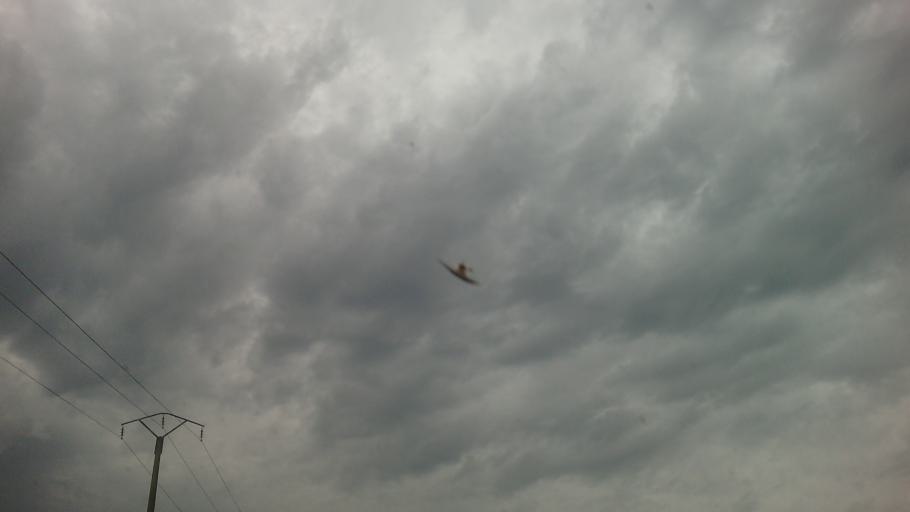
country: BJ
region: Mono
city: Lokossa
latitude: 6.5725
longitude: 1.7896
